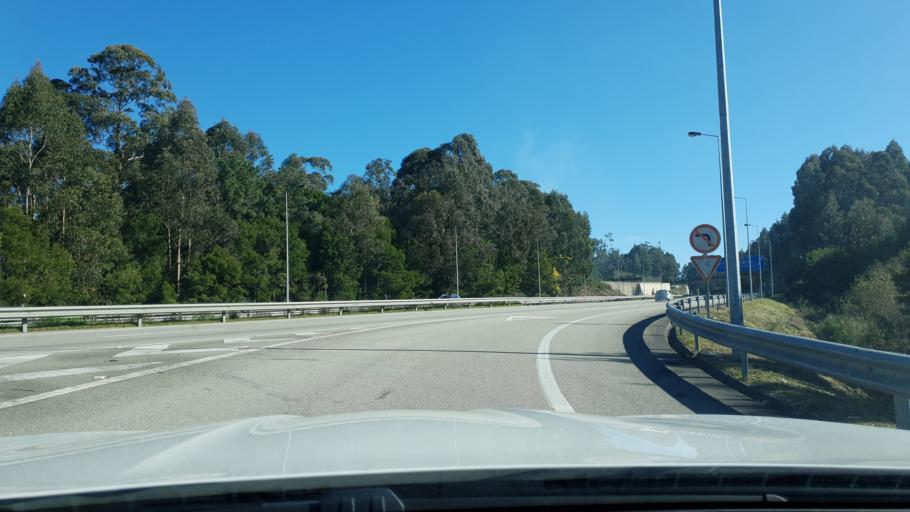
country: PT
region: Aveiro
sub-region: Santa Maria da Feira
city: Nogueira da Regedoura
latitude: 41.0082
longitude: -8.6040
